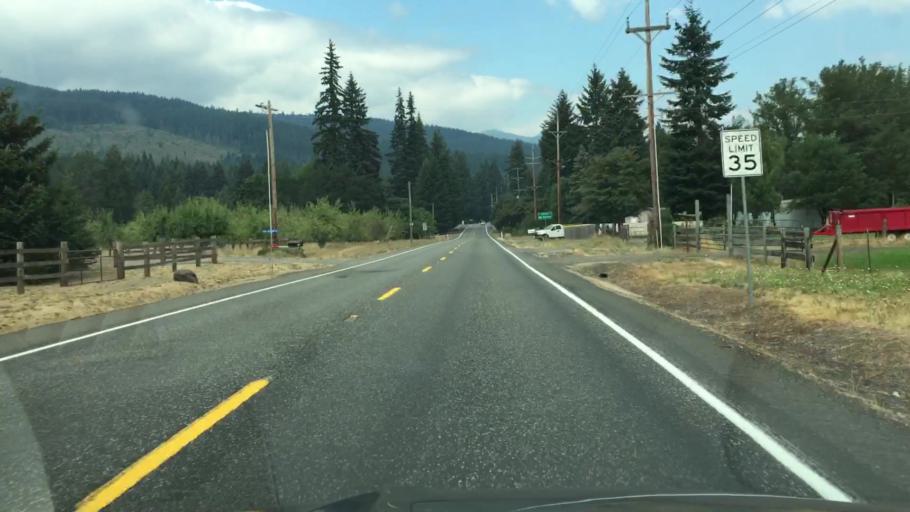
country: US
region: Washington
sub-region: Klickitat County
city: White Salmon
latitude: 45.8461
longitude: -121.5065
